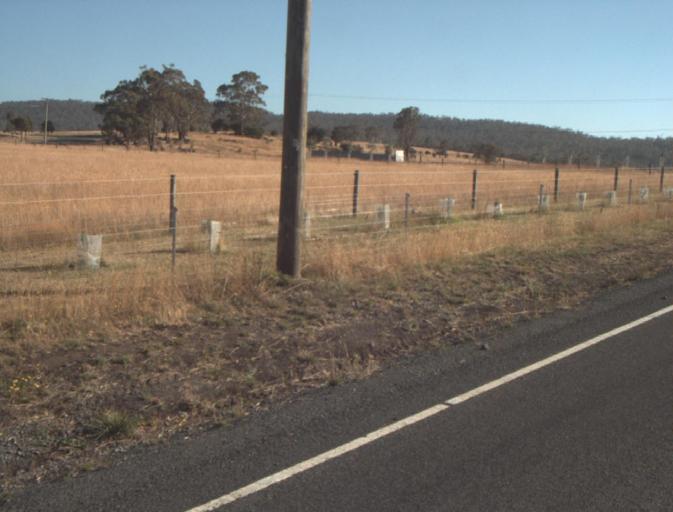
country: AU
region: Tasmania
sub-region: Launceston
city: Newstead
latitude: -41.4451
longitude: 147.2305
